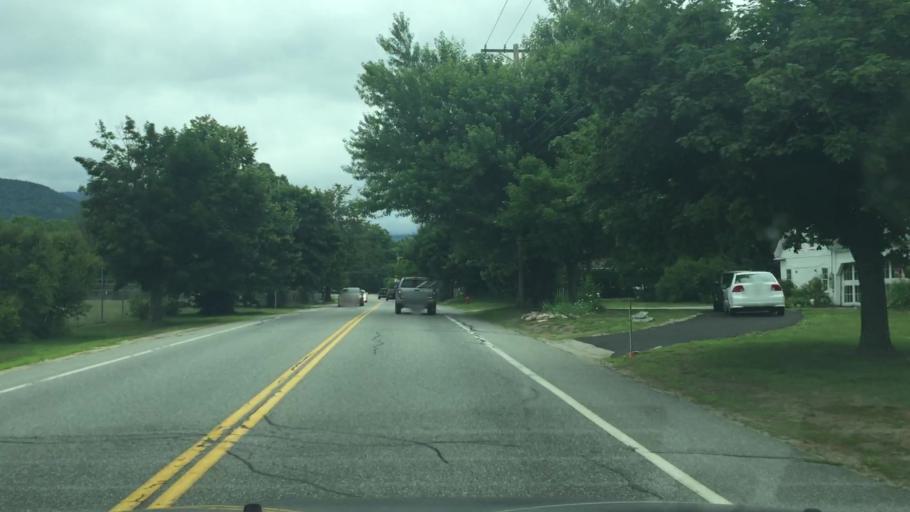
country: US
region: New Hampshire
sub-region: Carroll County
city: North Conway
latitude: 44.0782
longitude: -71.2785
